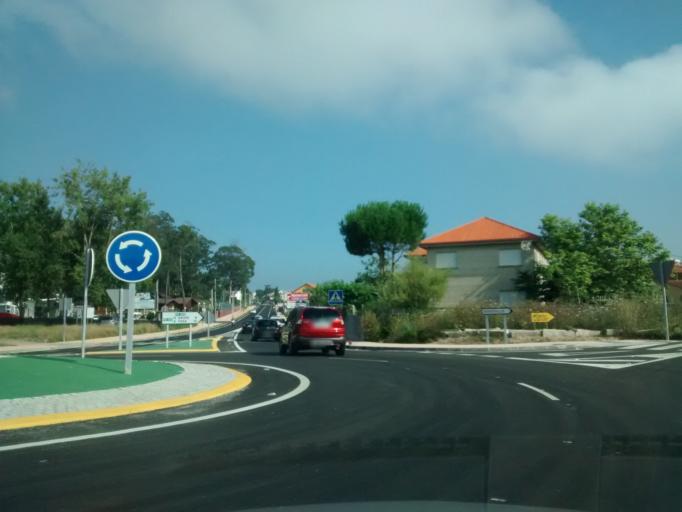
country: ES
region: Galicia
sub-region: Provincia de Pontevedra
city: Sanxenxo
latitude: 42.4166
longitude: -8.8682
